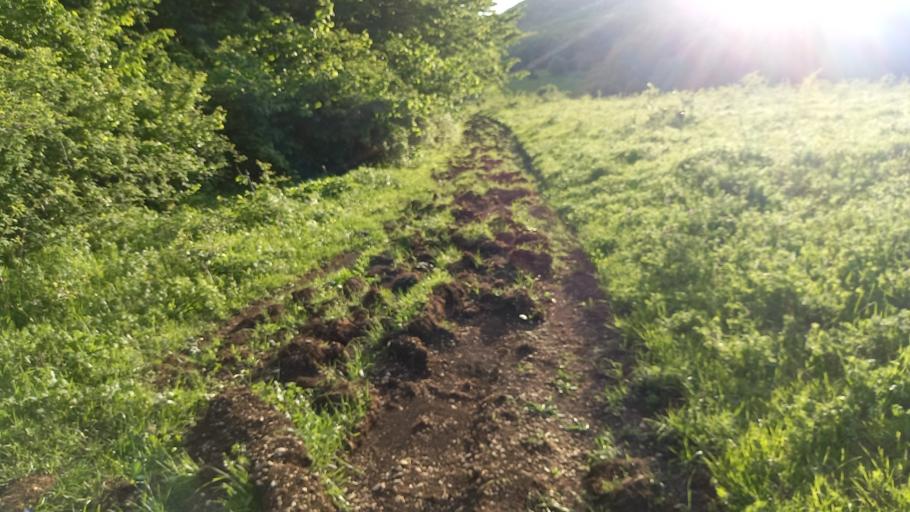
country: RU
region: Adygeya
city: Kamennomostskiy
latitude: 44.2193
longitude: 40.0031
